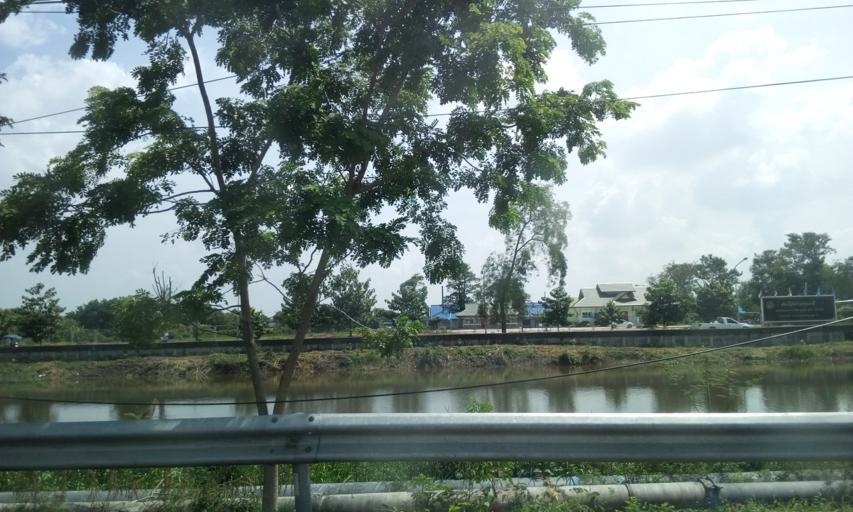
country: TH
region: Pathum Thani
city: Thanyaburi
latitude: 14.0183
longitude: 100.7304
